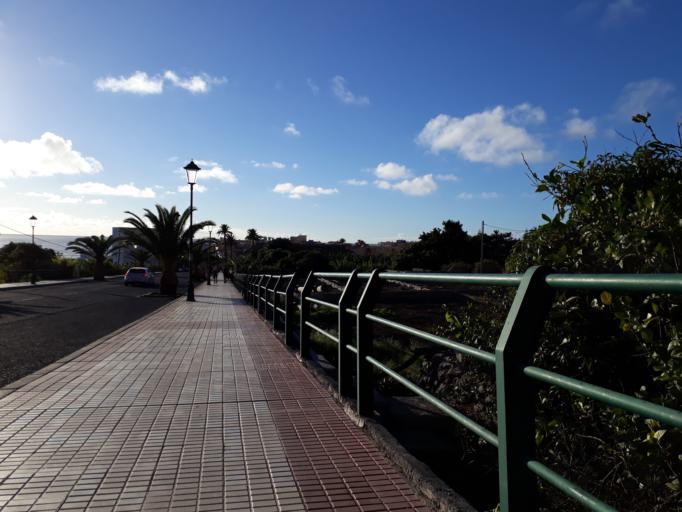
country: ES
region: Canary Islands
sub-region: Provincia de Santa Cruz de Tenerife
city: Alajero
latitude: 28.0950
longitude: -17.3388
